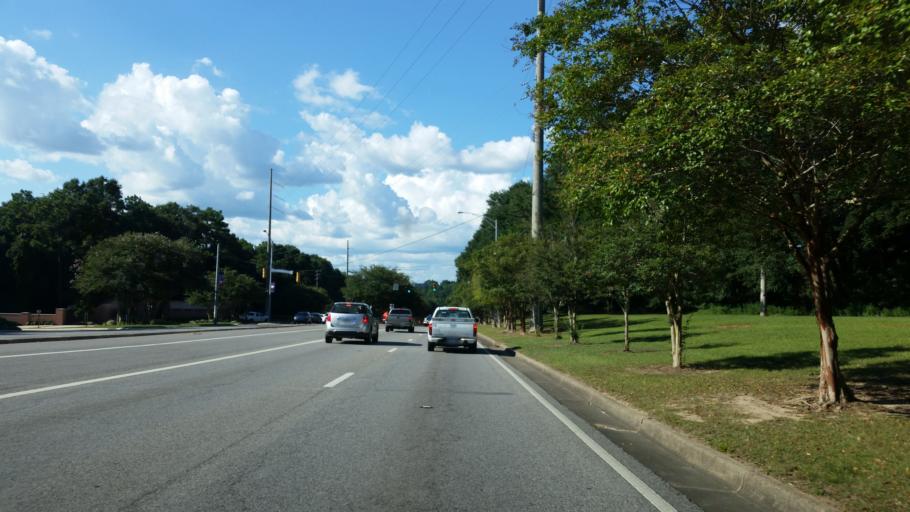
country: US
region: Alabama
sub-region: Mobile County
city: Prichard
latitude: 30.7003
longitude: -88.1741
